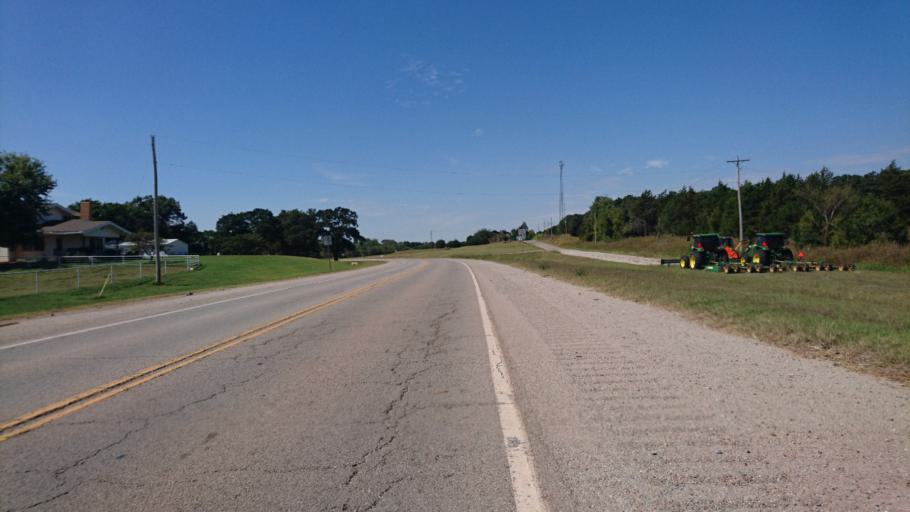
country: US
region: Oklahoma
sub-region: Oklahoma County
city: Jones
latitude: 35.6669
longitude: -97.3145
